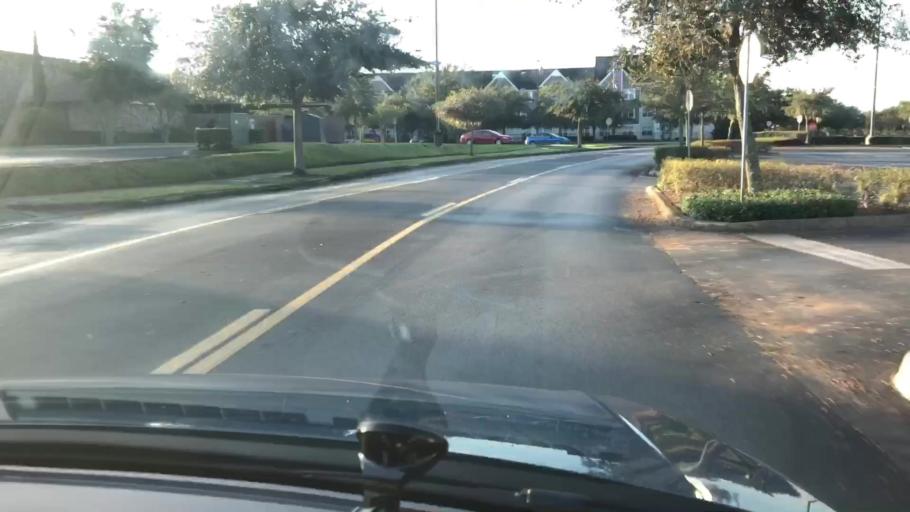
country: US
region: Florida
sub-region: Polk County
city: Medulla
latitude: 28.0016
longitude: -81.9763
